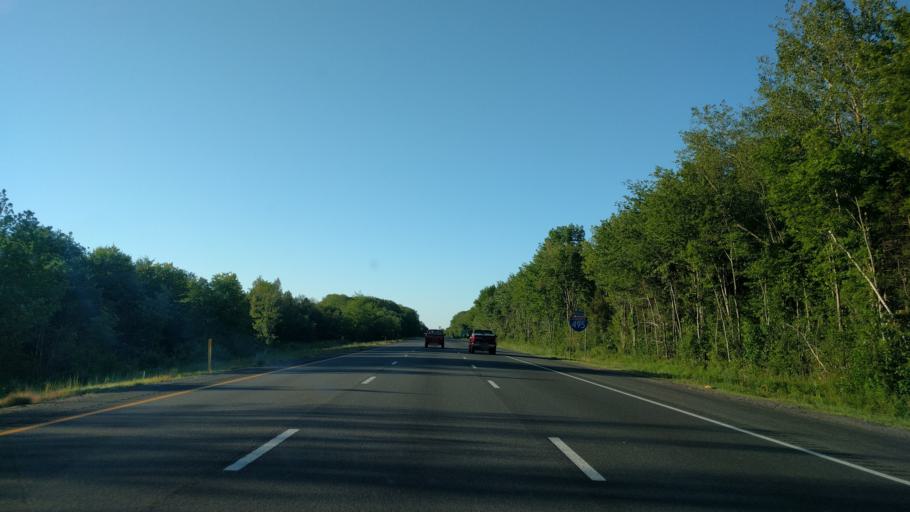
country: US
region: Massachusetts
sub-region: Worcester County
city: Milford
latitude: 42.1399
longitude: -71.4815
